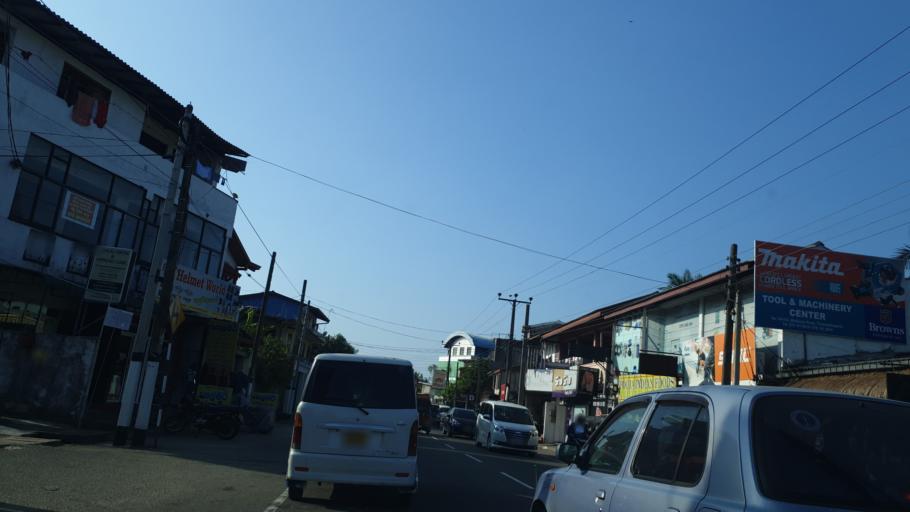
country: LK
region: Western
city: Battaramulla South
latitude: 6.8752
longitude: 79.9326
